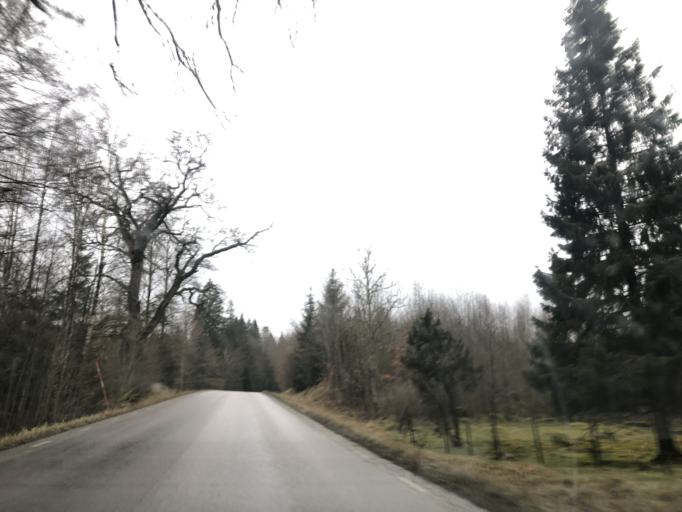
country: SE
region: Vaestra Goetaland
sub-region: Ulricehamns Kommun
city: Ulricehamn
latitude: 57.8332
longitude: 13.3157
